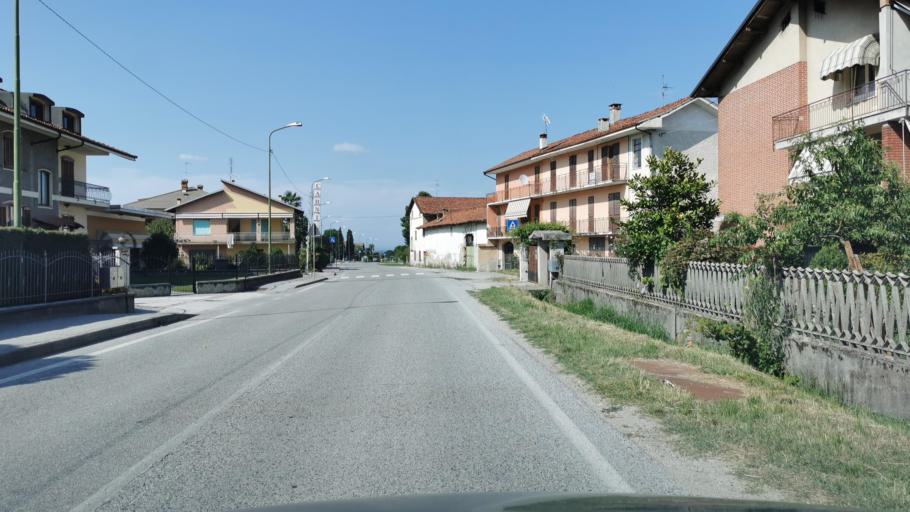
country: IT
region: Piedmont
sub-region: Provincia di Cuneo
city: Revello
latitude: 44.6577
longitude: 7.3932
